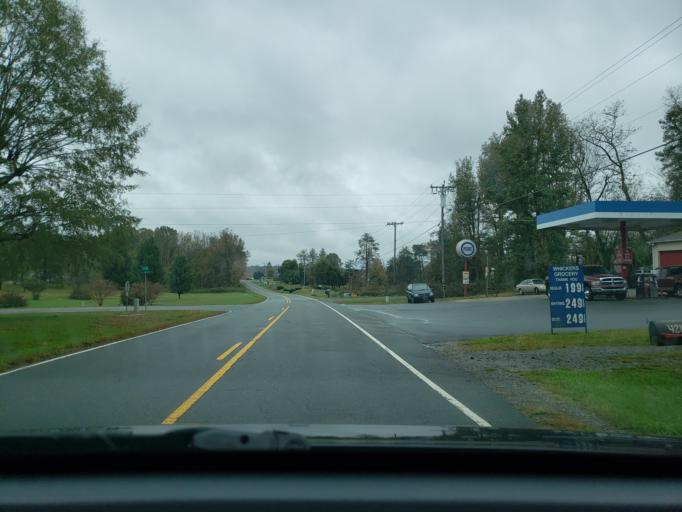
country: US
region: North Carolina
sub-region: Stokes County
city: Walnut Cove
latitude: 36.3380
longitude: -80.1514
